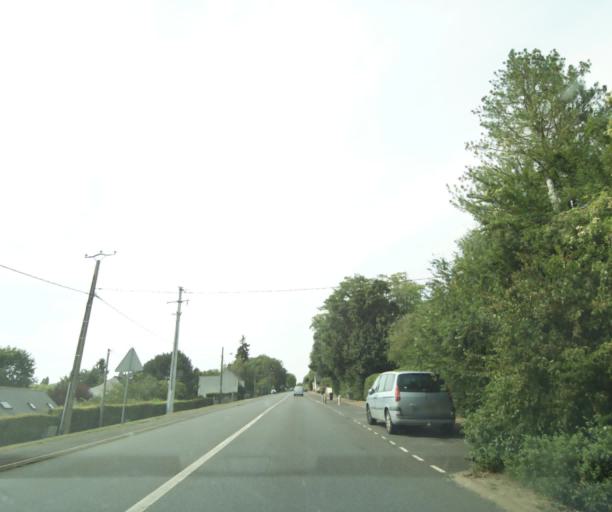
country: FR
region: Centre
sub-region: Departement d'Indre-et-Loire
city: La Membrolle-sur-Choisille
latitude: 47.4420
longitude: 0.6371
